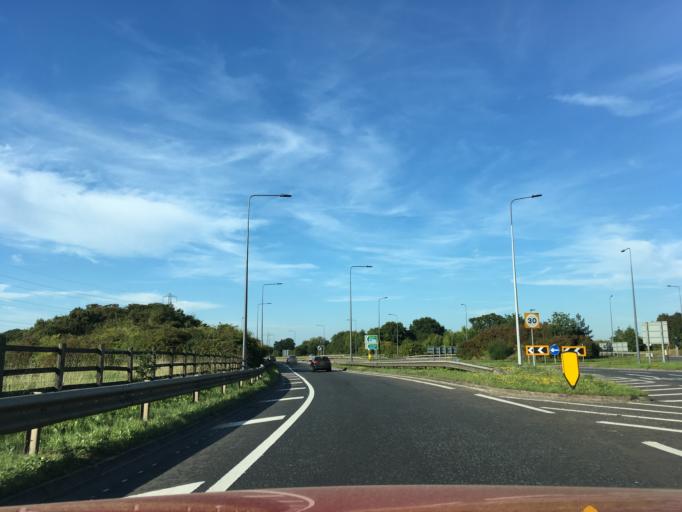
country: GB
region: England
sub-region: South Gloucestershire
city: Siston
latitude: 51.4858
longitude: -2.4704
